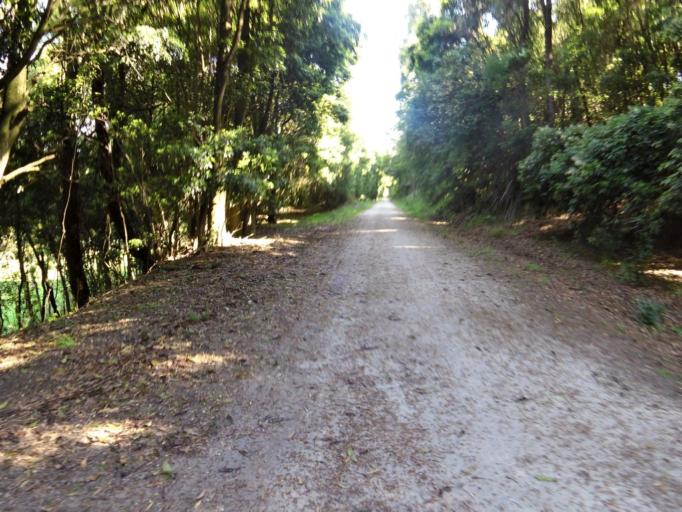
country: AU
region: Victoria
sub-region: Latrobe
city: Morwell
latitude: -38.6790
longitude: 146.1593
